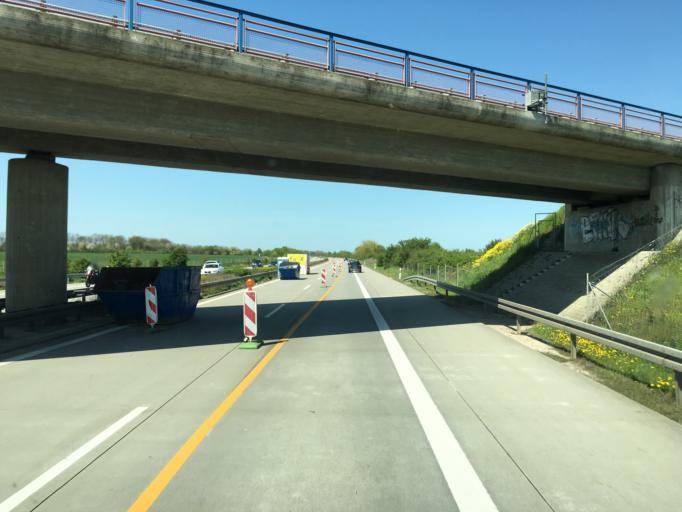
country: DE
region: Saxony-Anhalt
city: Lutzen
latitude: 51.2374
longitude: 12.1781
